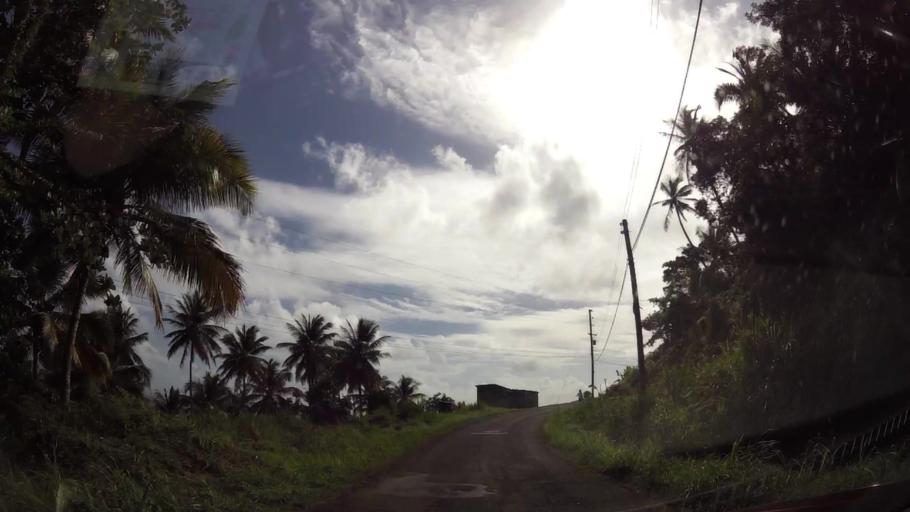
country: DM
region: Saint David
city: Castle Bruce
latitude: 15.4684
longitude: -61.2485
